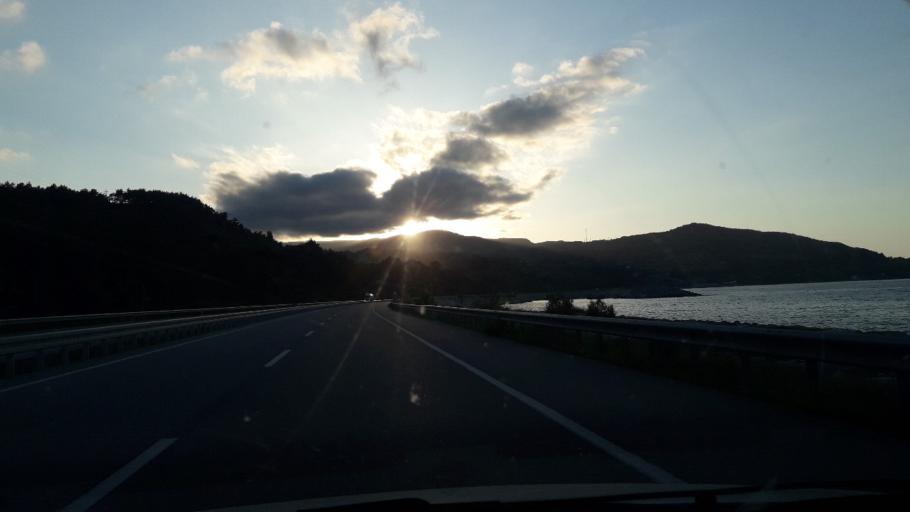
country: TR
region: Sinop
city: Dikmen
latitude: 41.7130
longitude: 35.2836
